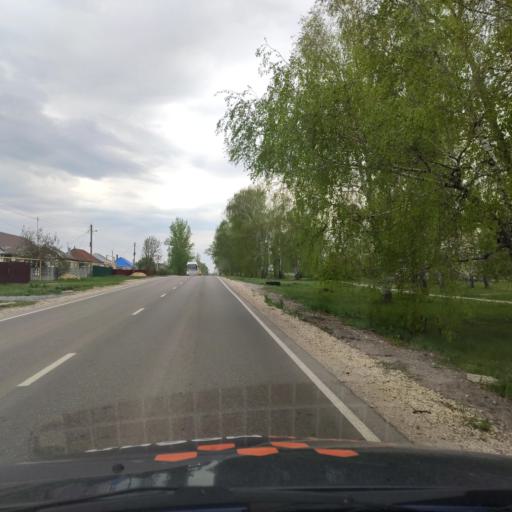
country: RU
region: Voronezj
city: Podgornoye
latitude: 51.8820
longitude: 39.1728
